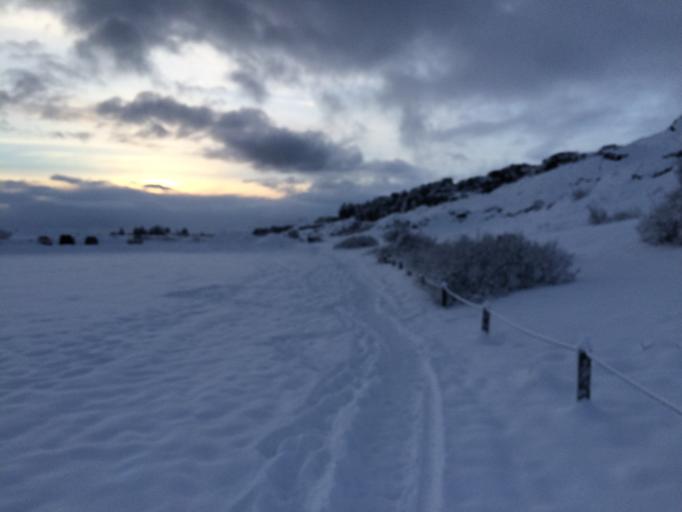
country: IS
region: South
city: Hveragerdi
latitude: 64.2642
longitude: -21.1169
